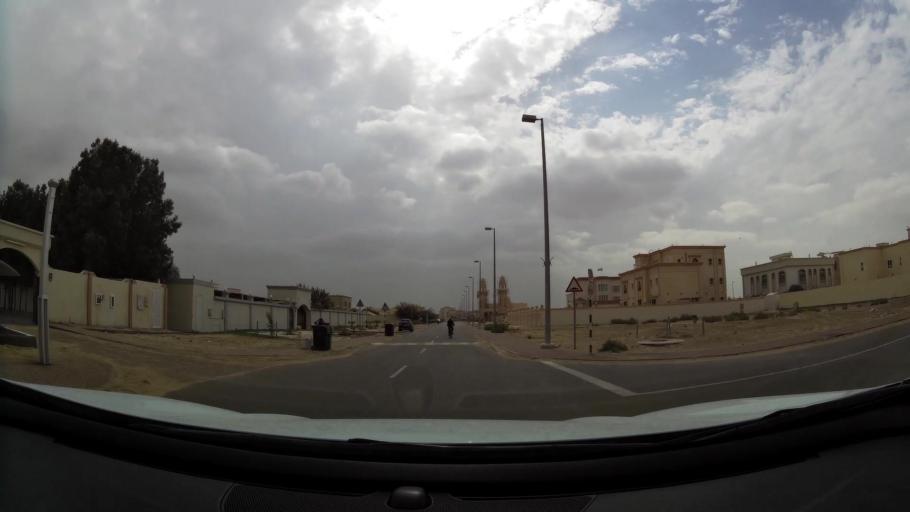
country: AE
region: Abu Dhabi
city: Abu Dhabi
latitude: 24.3856
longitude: 54.6428
